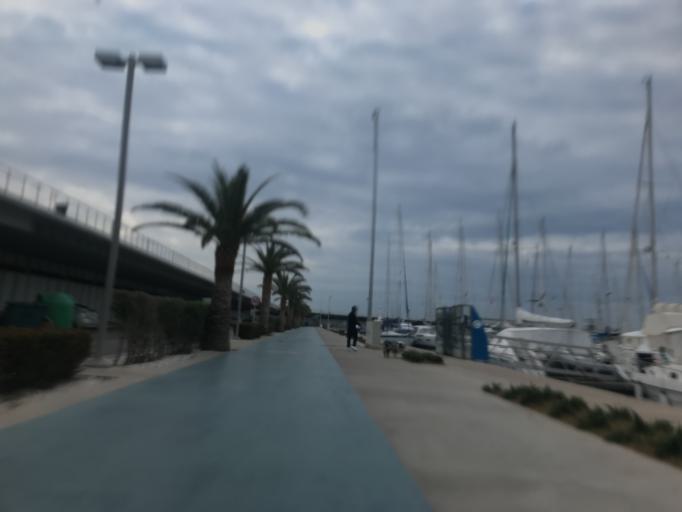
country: ES
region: Valencia
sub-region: Provincia de Valencia
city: Alboraya
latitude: 39.4625
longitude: -0.3149
